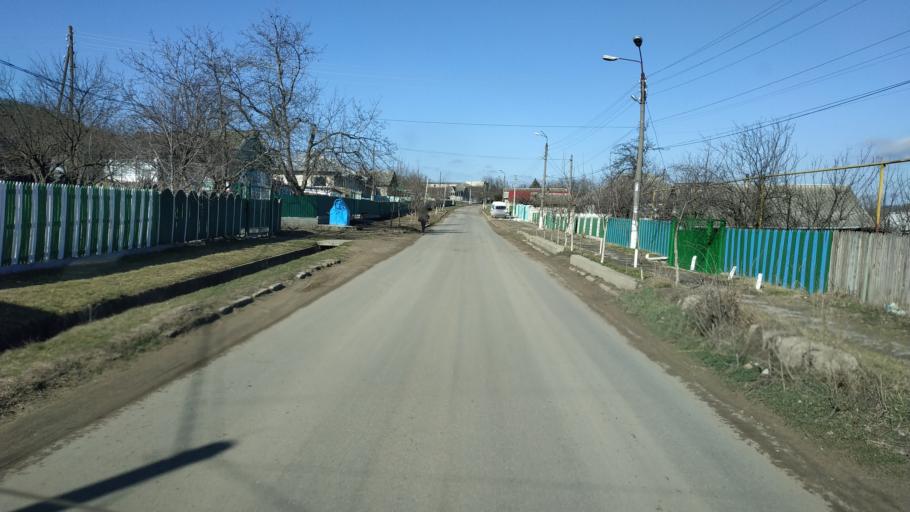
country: MD
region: Hincesti
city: Hincesti
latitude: 46.9664
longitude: 28.5961
